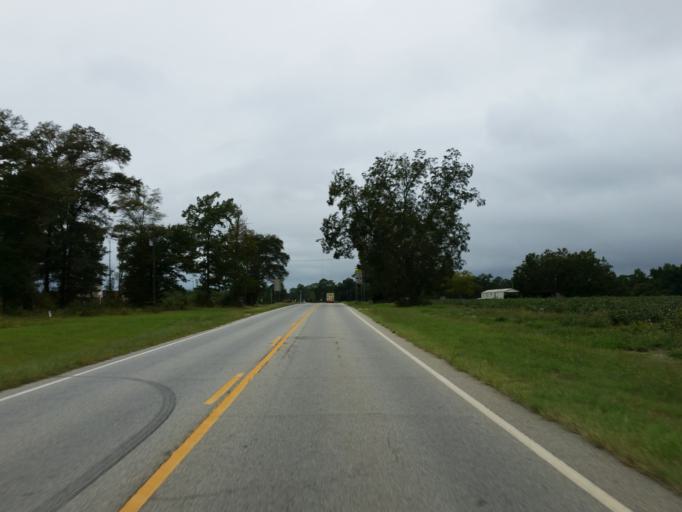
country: US
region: Georgia
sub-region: Cook County
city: Adel
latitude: 31.1342
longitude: -83.3811
